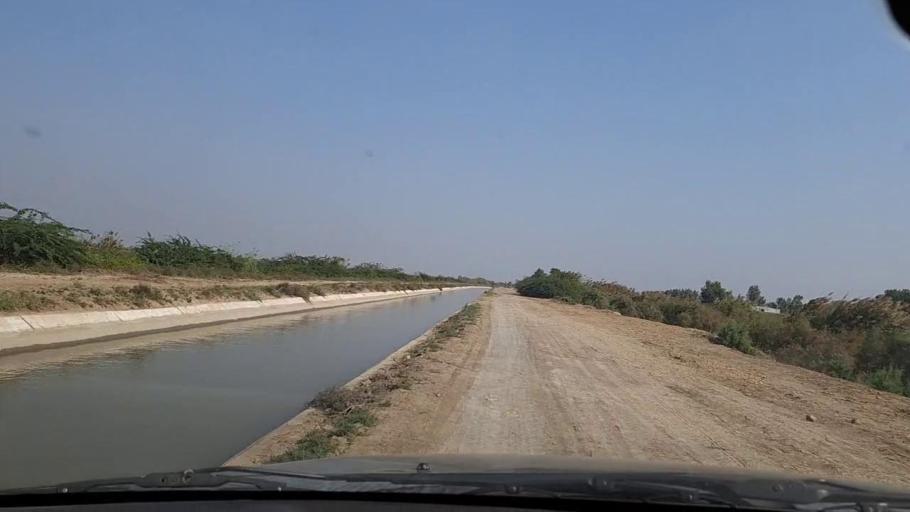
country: PK
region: Sindh
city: Mirpur Sakro
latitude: 24.3421
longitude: 67.7019
